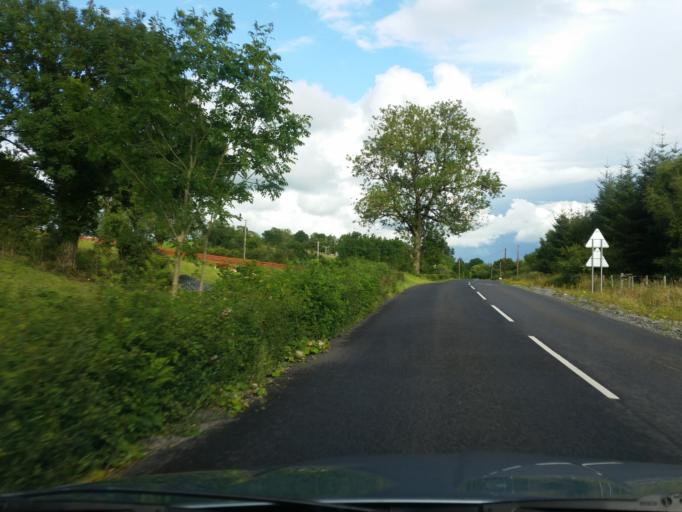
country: IE
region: Ulster
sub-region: County Monaghan
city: Clones
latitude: 54.1734
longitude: -7.2988
